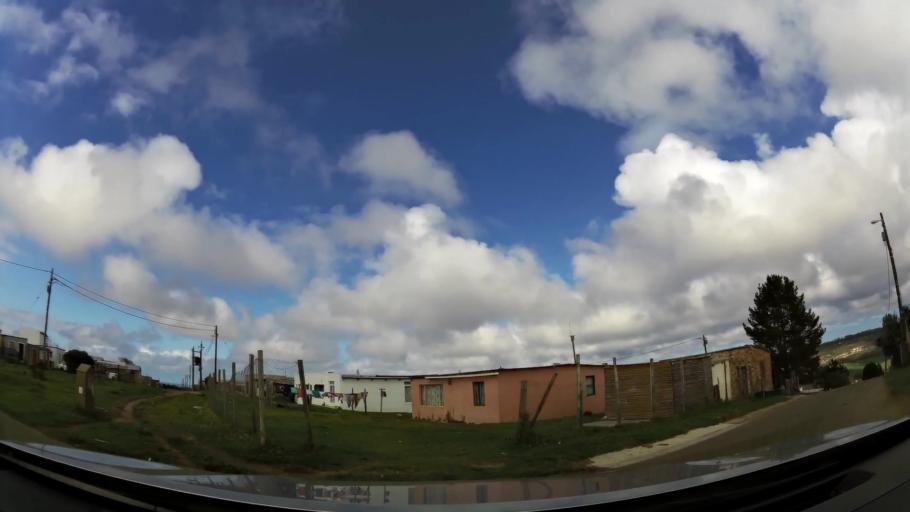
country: ZA
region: Western Cape
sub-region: Eden District Municipality
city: Plettenberg Bay
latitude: -34.0569
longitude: 23.3159
